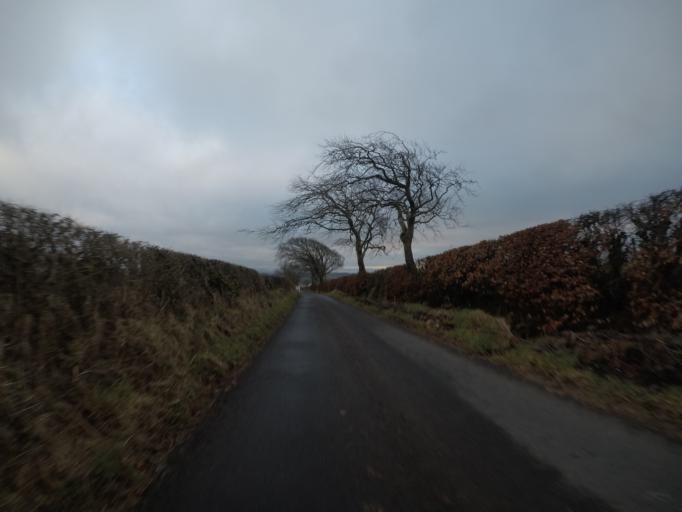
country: GB
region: Scotland
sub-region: North Ayrshire
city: Dalry
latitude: 55.7220
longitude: -4.7612
